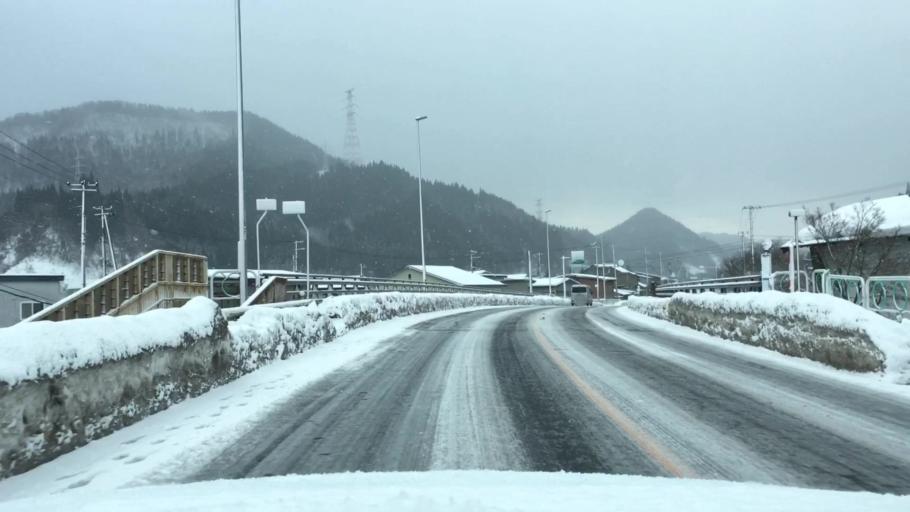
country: JP
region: Aomori
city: Kuroishi
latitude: 40.4704
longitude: 140.6326
